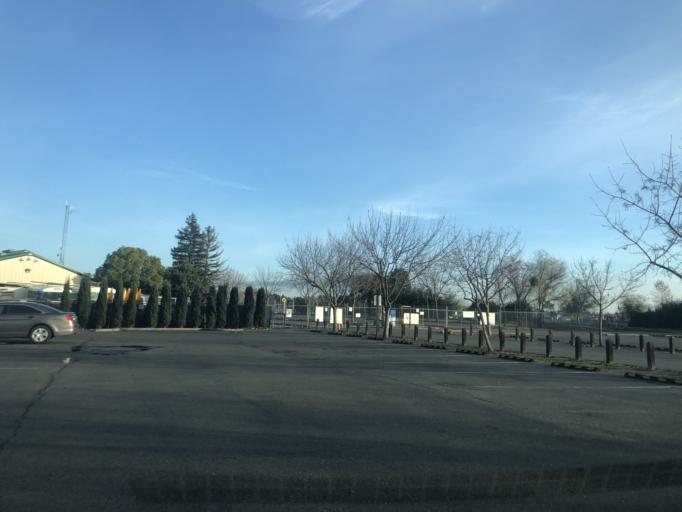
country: US
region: California
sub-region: Sacramento County
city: Gold River
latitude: 38.6344
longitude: -121.2205
